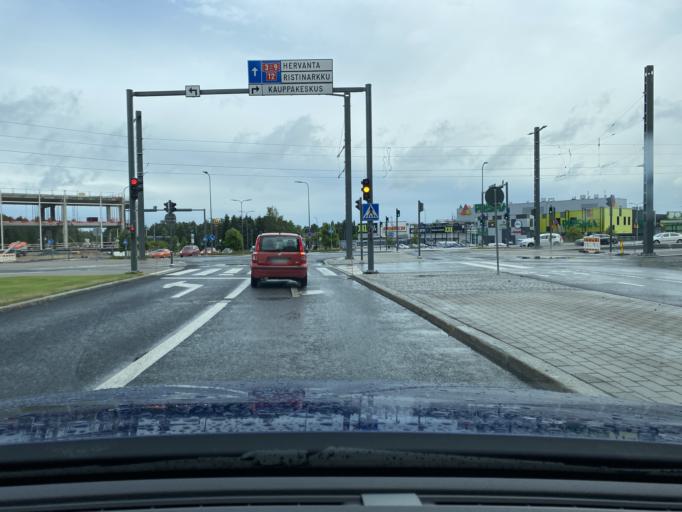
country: FI
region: Pirkanmaa
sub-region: Tampere
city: Tampere
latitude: 61.4934
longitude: 23.8174
